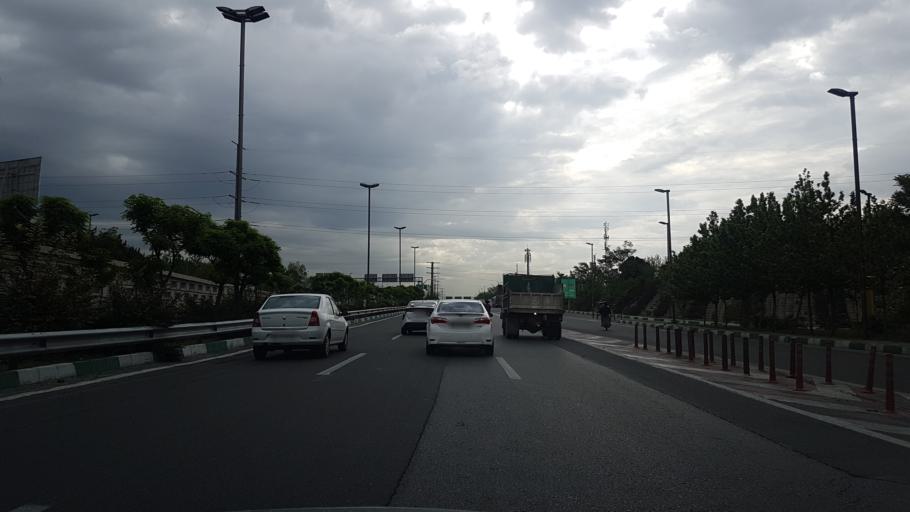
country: IR
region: Tehran
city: Tehran
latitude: 35.7398
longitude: 51.4203
